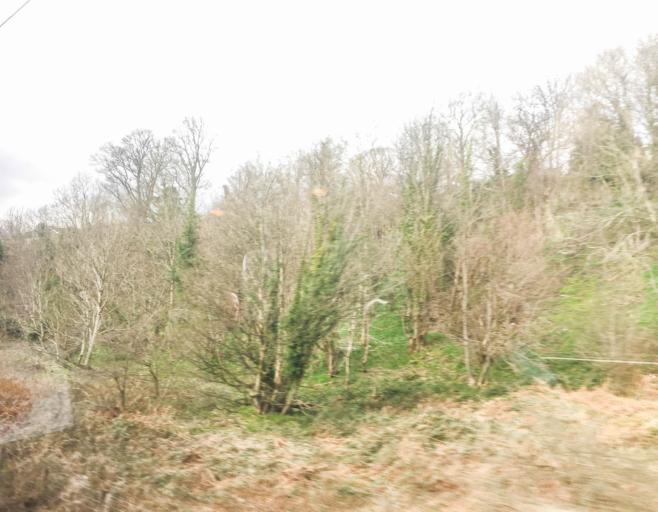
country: GB
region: Scotland
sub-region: West Dunbartonshire
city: Renton
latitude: 55.9474
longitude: -4.6046
